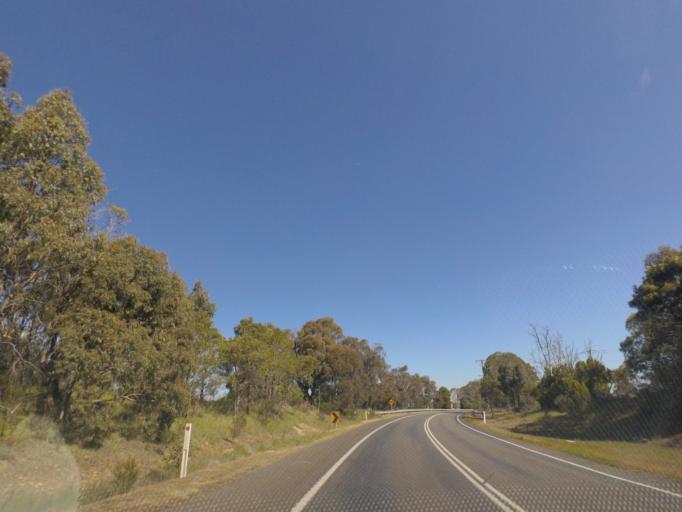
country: AU
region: Victoria
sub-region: Whittlesea
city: Whittlesea
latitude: -37.3294
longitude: 144.9837
